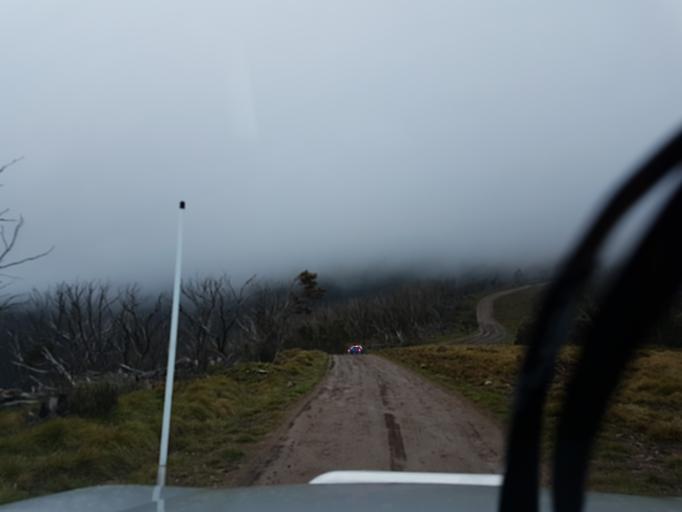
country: AU
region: Victoria
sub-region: Alpine
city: Mount Beauty
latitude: -37.0863
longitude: 147.1067
